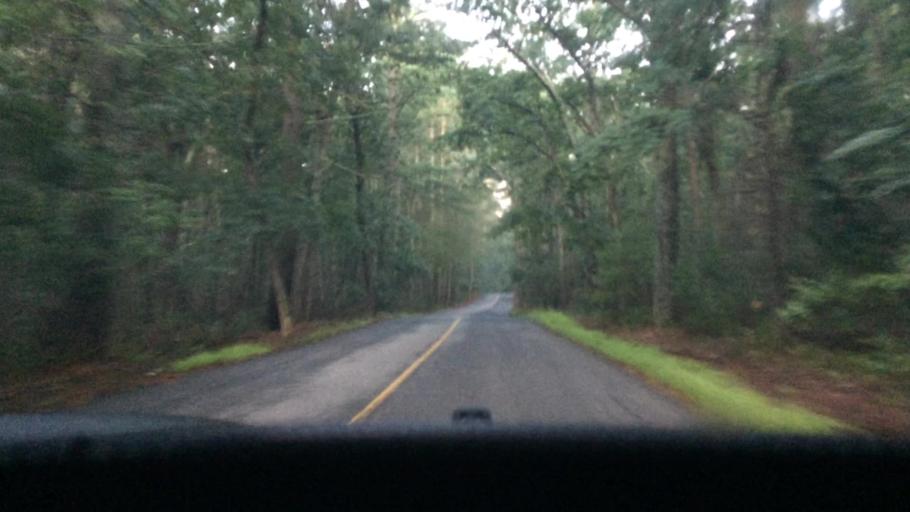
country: US
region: Massachusetts
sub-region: Middlesex County
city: North Reading
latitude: 42.6110
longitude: -71.1130
